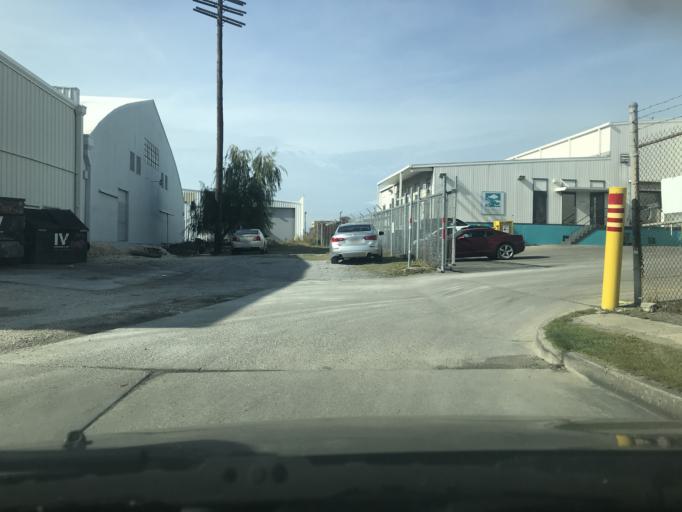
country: US
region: Louisiana
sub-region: Orleans Parish
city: New Orleans
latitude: 29.9583
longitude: -90.0977
